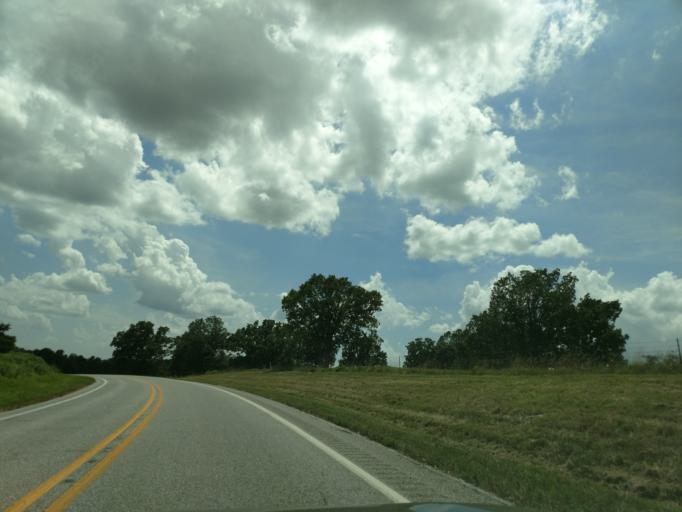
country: US
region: Arkansas
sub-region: Boone County
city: Harrison
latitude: 36.2104
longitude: -92.9325
